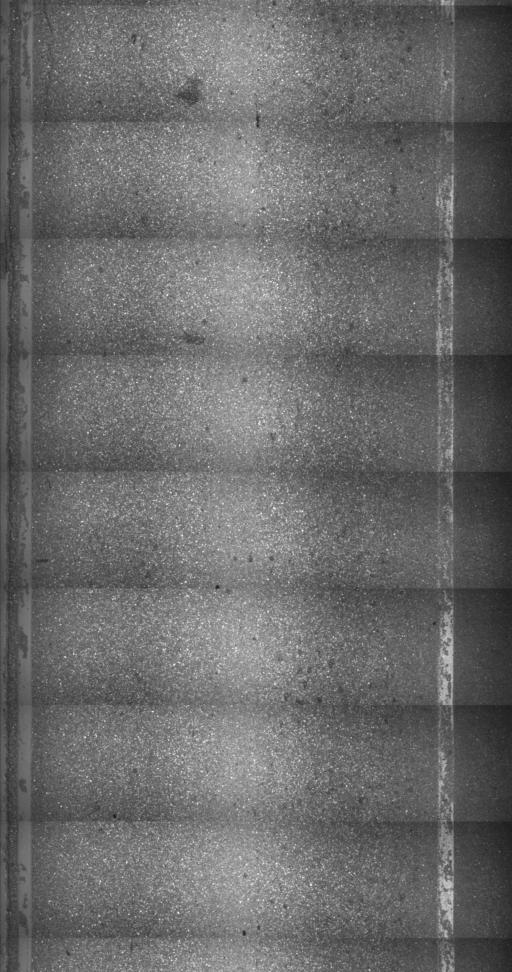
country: US
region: Vermont
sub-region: Franklin County
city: Saint Albans
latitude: 44.7302
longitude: -73.1172
